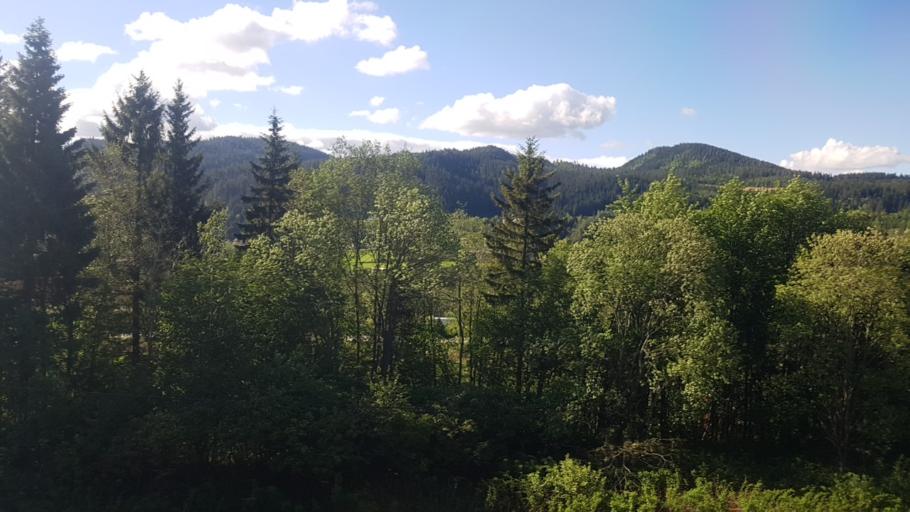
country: NO
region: Sor-Trondelag
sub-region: Midtre Gauldal
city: Storen
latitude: 63.0322
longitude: 10.2775
